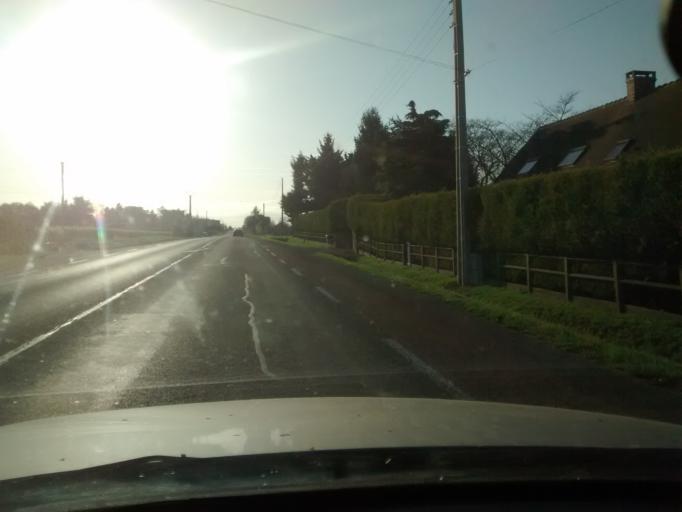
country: FR
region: Pays de la Loire
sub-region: Departement de la Sarthe
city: Trange
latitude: 48.0237
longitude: 0.0882
